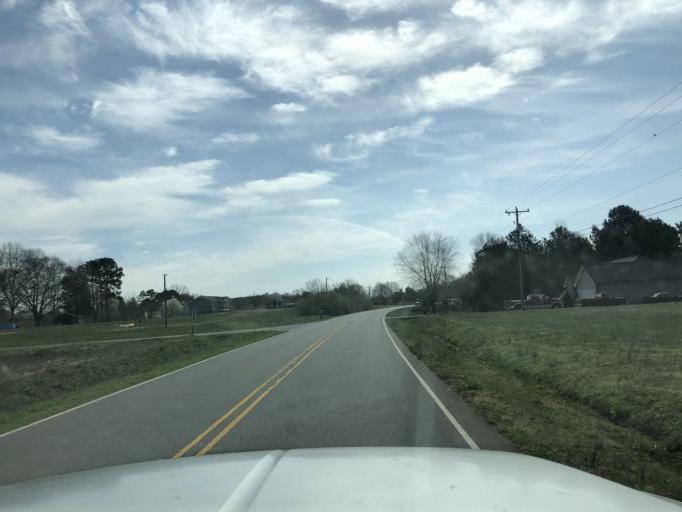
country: US
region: North Carolina
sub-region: Cleveland County
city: Shelby
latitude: 35.3782
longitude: -81.6056
